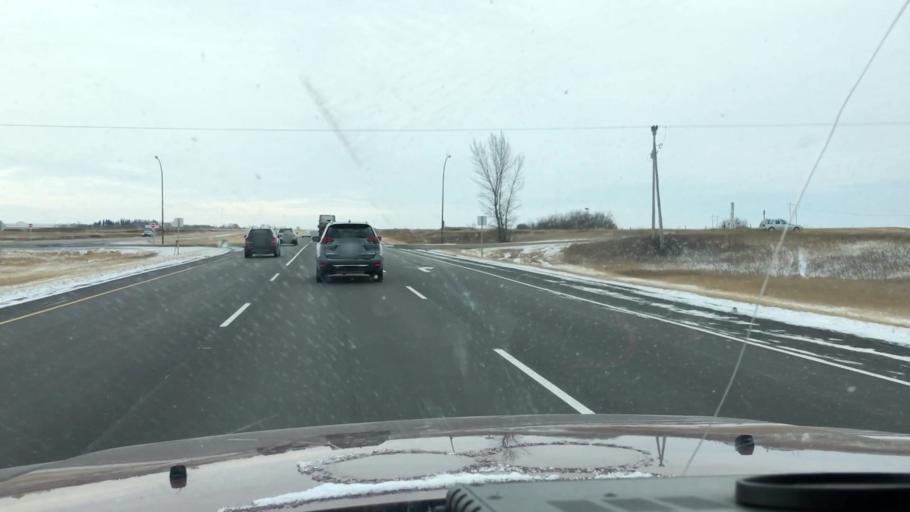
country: CA
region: Saskatchewan
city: Saskatoon
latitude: 51.8534
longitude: -106.5112
